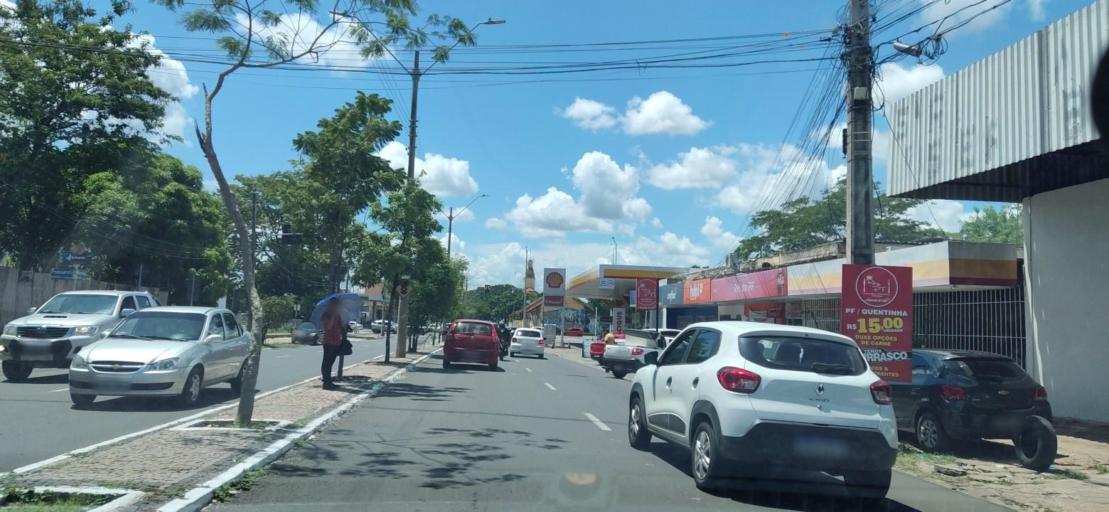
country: BR
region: Piaui
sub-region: Teresina
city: Teresina
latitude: -5.0874
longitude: -42.8025
